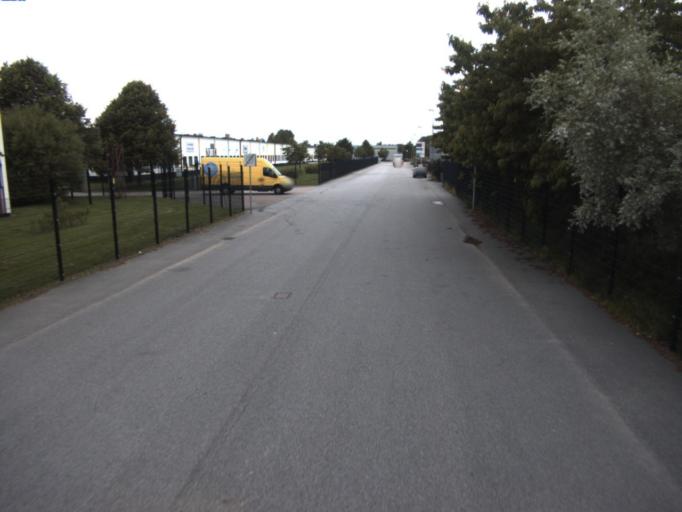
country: SE
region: Skane
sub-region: Helsingborg
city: Odakra
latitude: 56.0822
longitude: 12.7374
